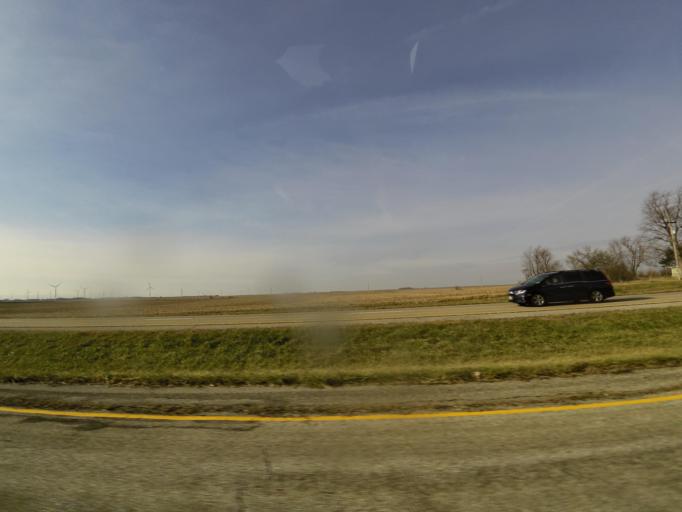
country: US
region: Illinois
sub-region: Macon County
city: Maroa
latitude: 40.0653
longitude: -88.9657
